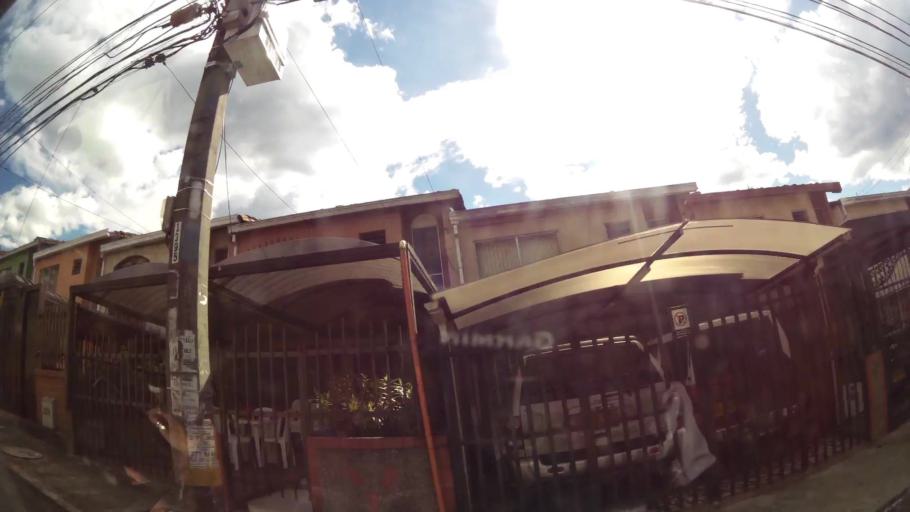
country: CO
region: Antioquia
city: Sabaneta
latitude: 6.1555
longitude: -75.6062
